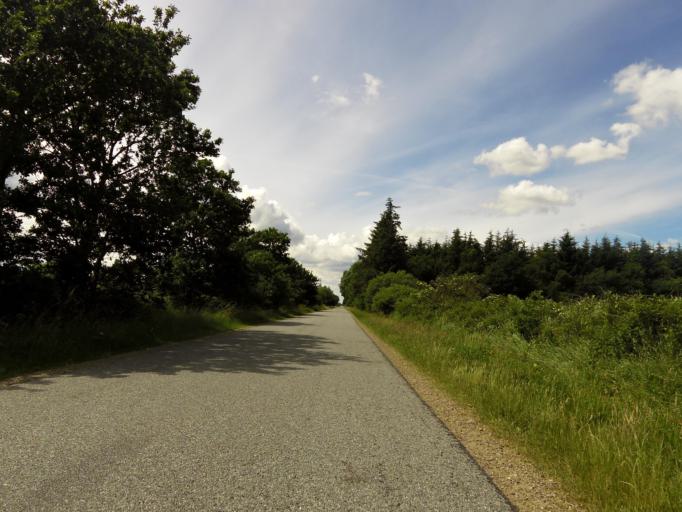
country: DK
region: South Denmark
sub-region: Esbjerg Kommune
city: Ribe
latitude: 55.2618
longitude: 8.8561
